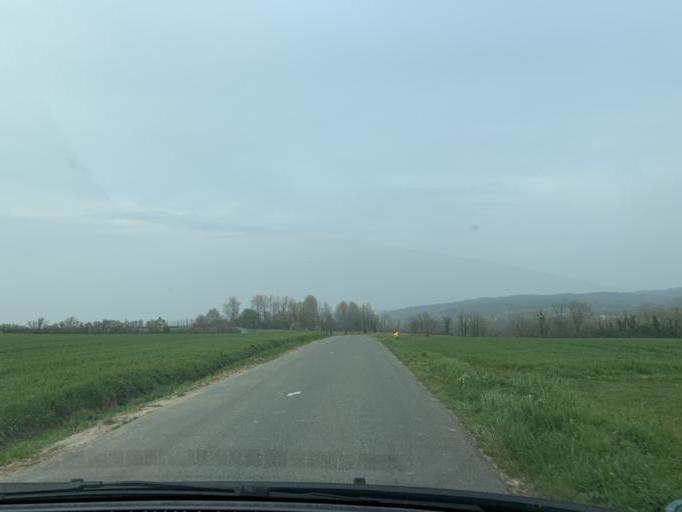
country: FR
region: Nord-Pas-de-Calais
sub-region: Departement du Pas-de-Calais
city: Longfosse
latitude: 50.6887
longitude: 1.7675
